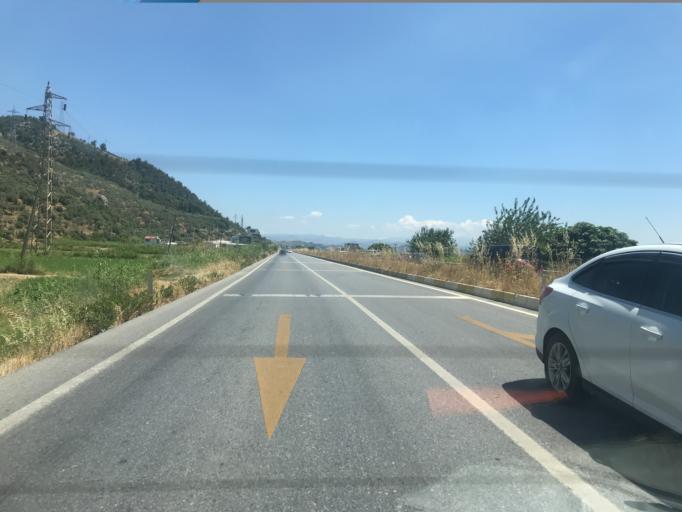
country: TR
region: Aydin
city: Soeke
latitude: 37.8001
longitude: 27.4722
